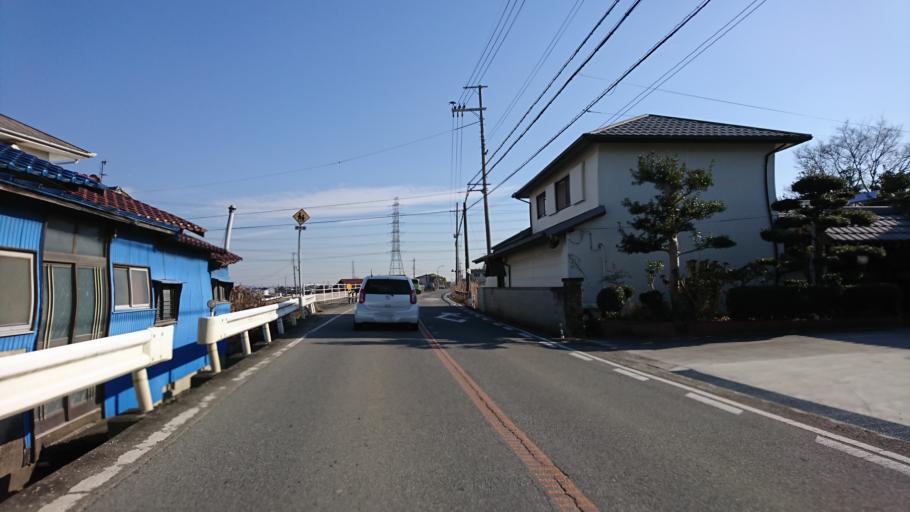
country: JP
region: Hyogo
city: Kakogawacho-honmachi
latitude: 34.8110
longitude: 134.8536
